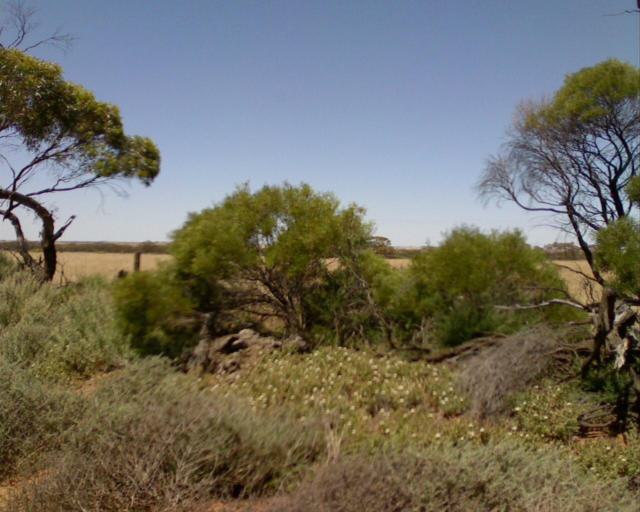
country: AU
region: South Australia
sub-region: Kimba
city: Caralue
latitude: -32.9460
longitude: 135.2807
